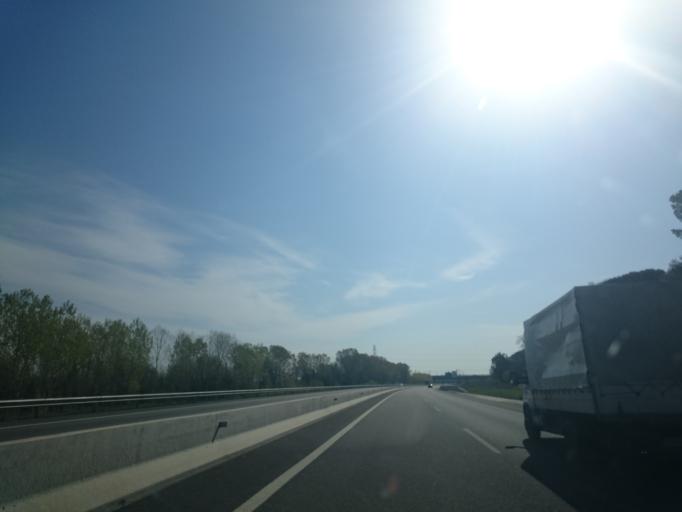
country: ES
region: Catalonia
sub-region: Provincia de Girona
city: Vilobi d'Onyar
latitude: 41.8754
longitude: 2.7525
